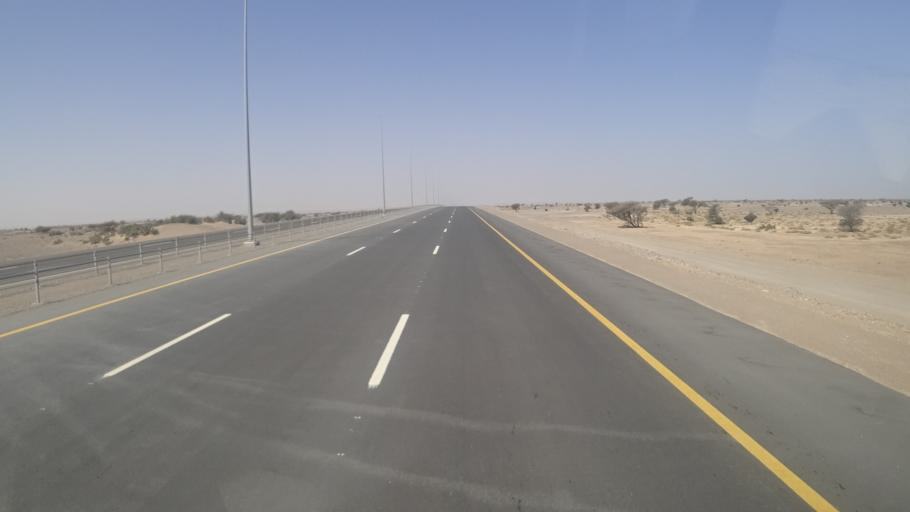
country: OM
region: Ash Sharqiyah
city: Badiyah
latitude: 22.2756
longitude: 59.2016
